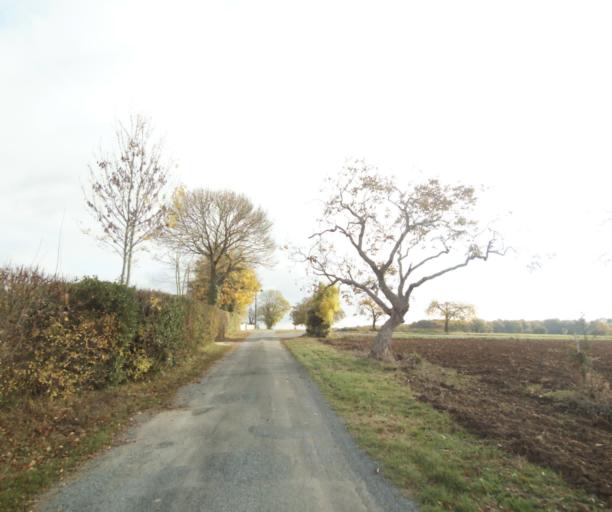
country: FR
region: Poitou-Charentes
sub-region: Departement de la Charente-Maritime
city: Saint-Georges-des-Coteaux
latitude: 45.7666
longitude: -0.6859
